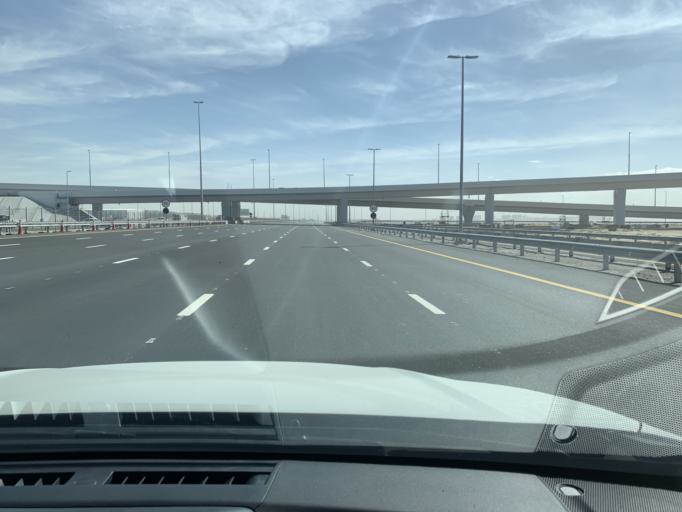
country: AE
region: Dubai
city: Dubai
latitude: 24.9642
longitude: 55.1829
